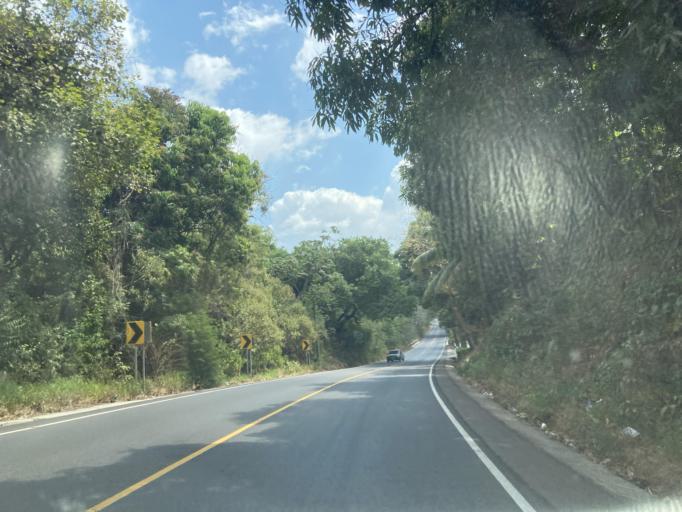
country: GT
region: Santa Rosa
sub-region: Municipio de Taxisco
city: Taxisco
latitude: 14.0653
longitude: -90.4569
